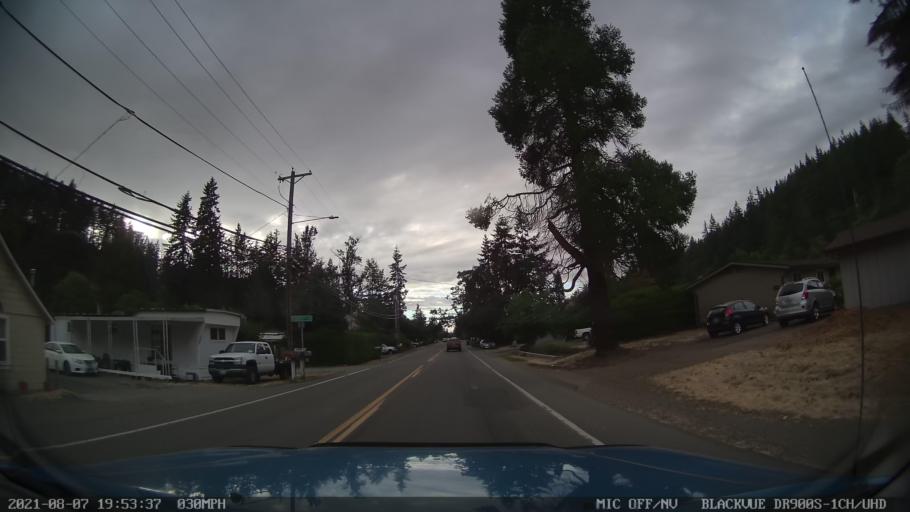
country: US
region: Oregon
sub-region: Marion County
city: Silverton
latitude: 44.9899
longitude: -122.7677
